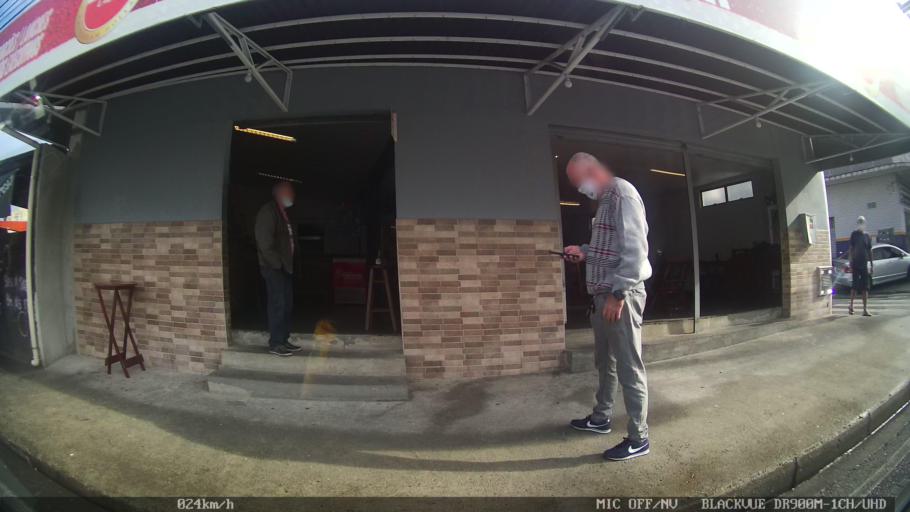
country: BR
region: Santa Catarina
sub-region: Sao Jose
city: Campinas
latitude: -27.6046
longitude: -48.6277
